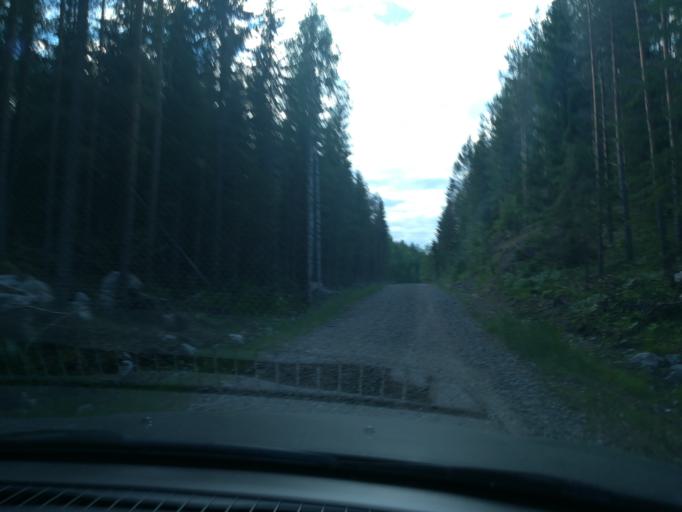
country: FI
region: Southern Savonia
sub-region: Mikkeli
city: Puumala
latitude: 61.6208
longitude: 28.1732
